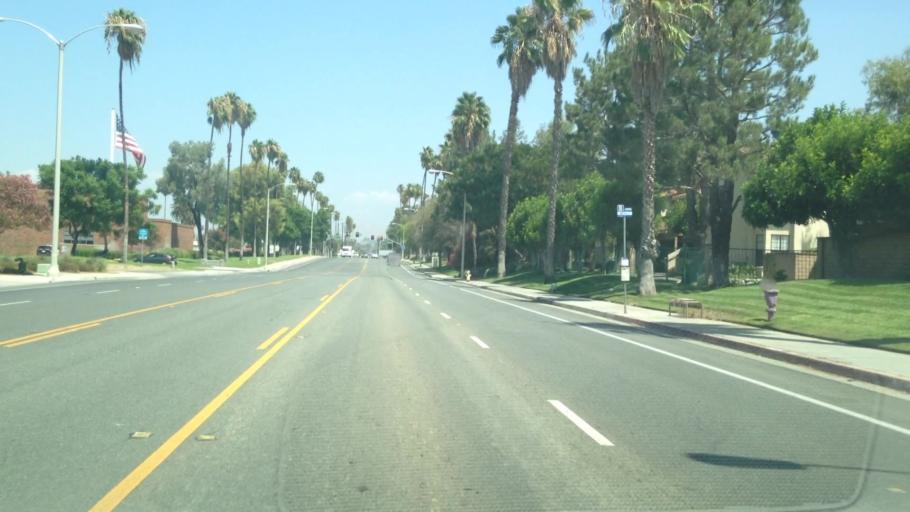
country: US
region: California
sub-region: Riverside County
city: Riverside
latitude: 33.9211
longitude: -117.4132
